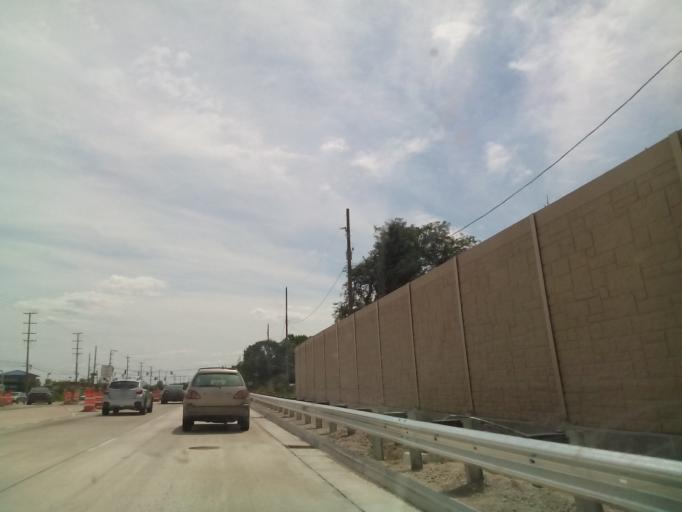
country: US
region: Illinois
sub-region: DuPage County
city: Warrenville
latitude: 41.7933
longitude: -88.2057
